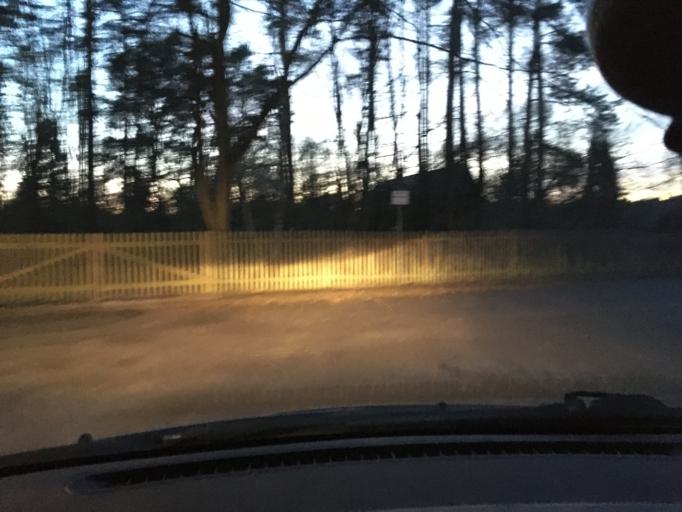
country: DE
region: Lower Saxony
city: Hanstedt
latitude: 53.2341
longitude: 10.0174
